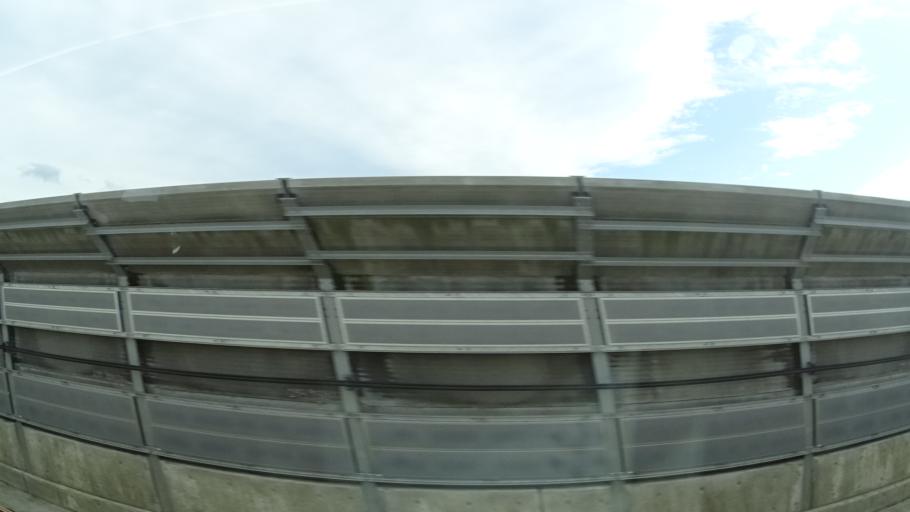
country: JP
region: Toyama
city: Kuragaki-kosugi
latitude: 36.7238
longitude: 137.1400
